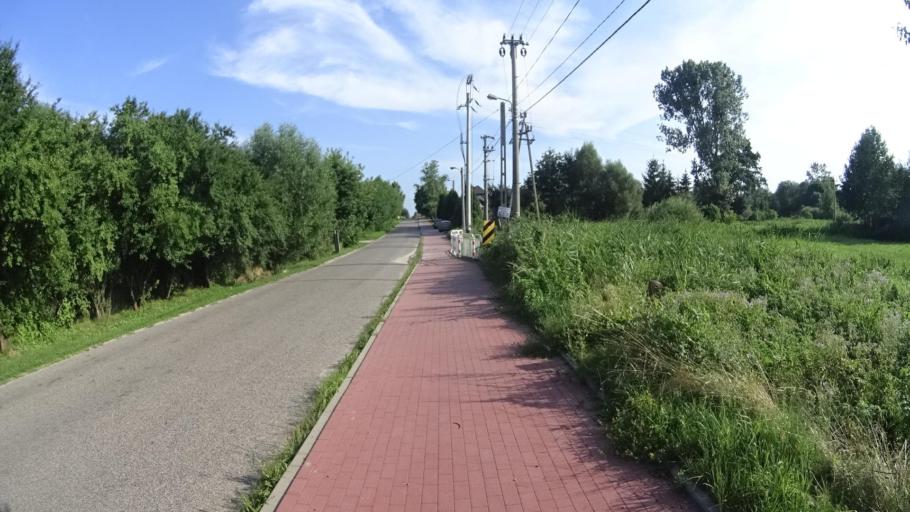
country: PL
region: Masovian Voivodeship
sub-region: Powiat pruszkowski
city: Nadarzyn
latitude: 52.0754
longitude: 20.7848
